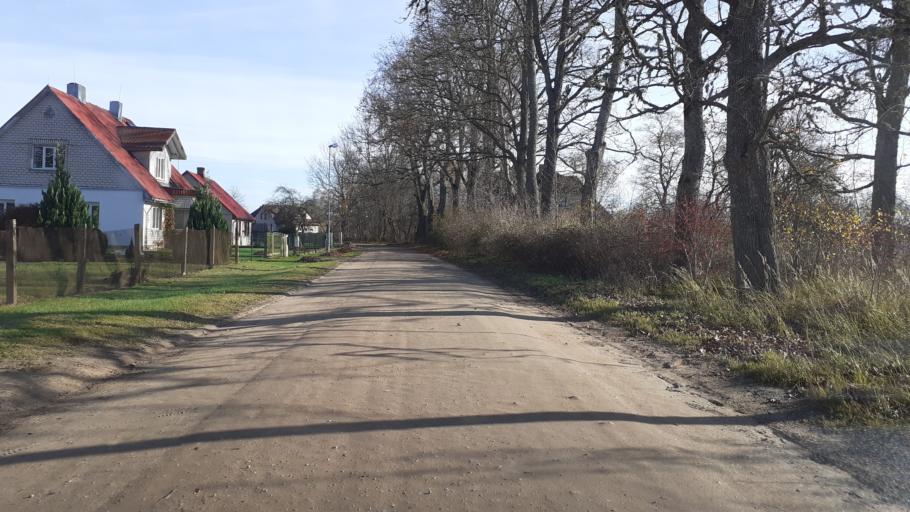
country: LV
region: Kuldigas Rajons
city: Kuldiga
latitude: 56.9586
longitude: 21.9940
